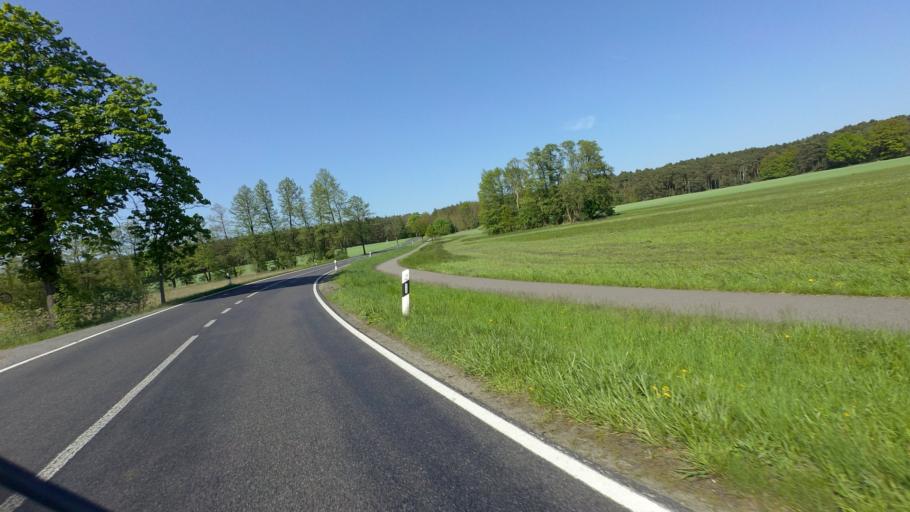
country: DE
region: Brandenburg
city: Neu Zauche
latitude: 52.0240
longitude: 14.0397
